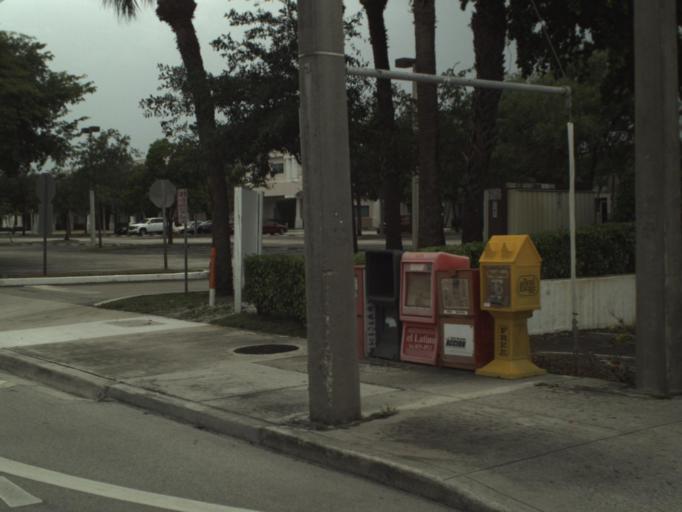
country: US
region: Florida
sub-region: Palm Beach County
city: Palm Beach
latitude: 26.6867
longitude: -80.0545
